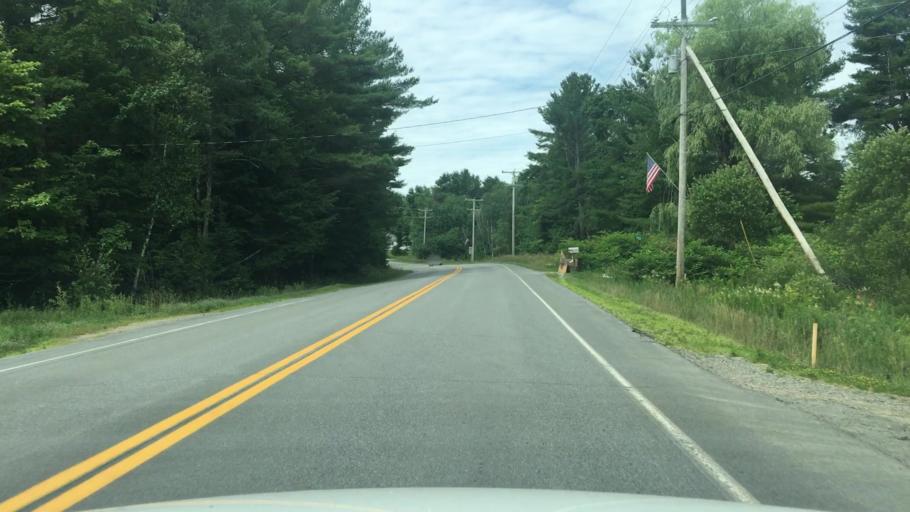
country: US
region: Maine
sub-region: Waldo County
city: Troy
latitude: 44.5331
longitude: -69.2882
